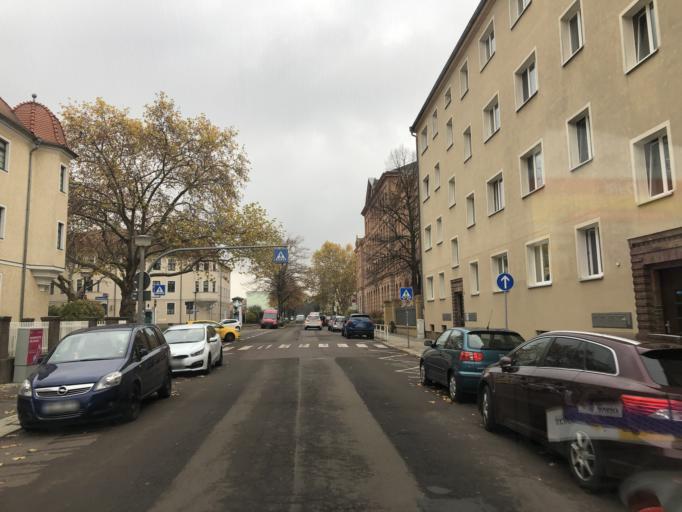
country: DE
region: Saxony-Anhalt
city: Halle (Saale)
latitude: 51.4707
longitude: 11.9736
